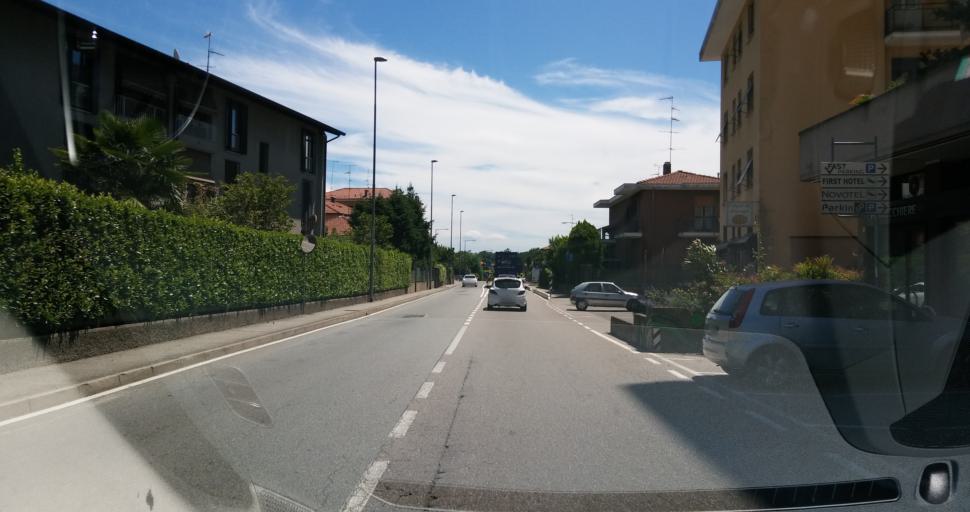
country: IT
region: Lombardy
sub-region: Provincia di Varese
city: Somma Lombardo
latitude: 45.6804
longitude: 8.7072
